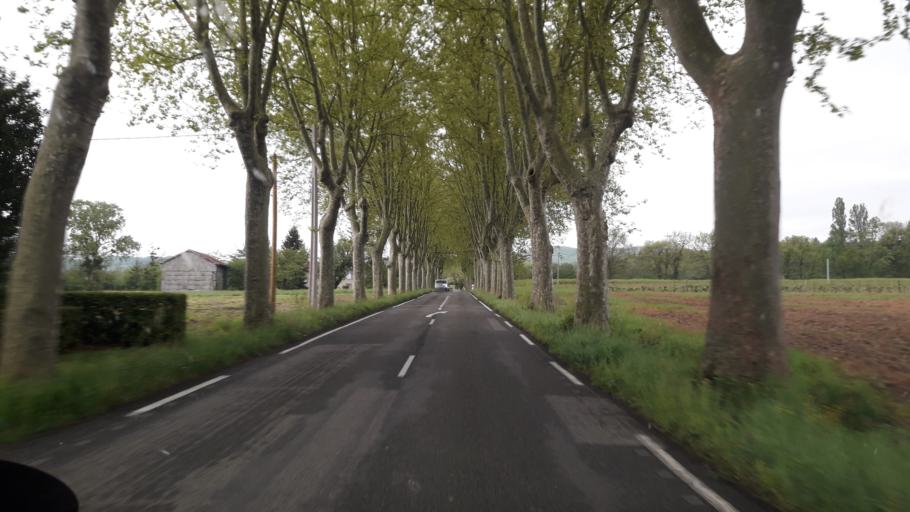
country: FR
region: Midi-Pyrenees
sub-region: Departement de la Haute-Garonne
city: Cazeres
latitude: 43.1912
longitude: 1.1054
